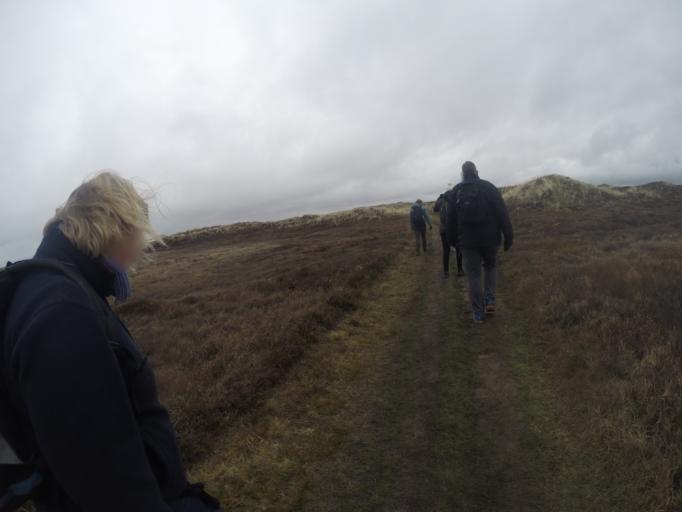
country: DK
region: Central Jutland
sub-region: Lemvig Kommune
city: Thyboron
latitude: 56.8288
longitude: 8.2649
